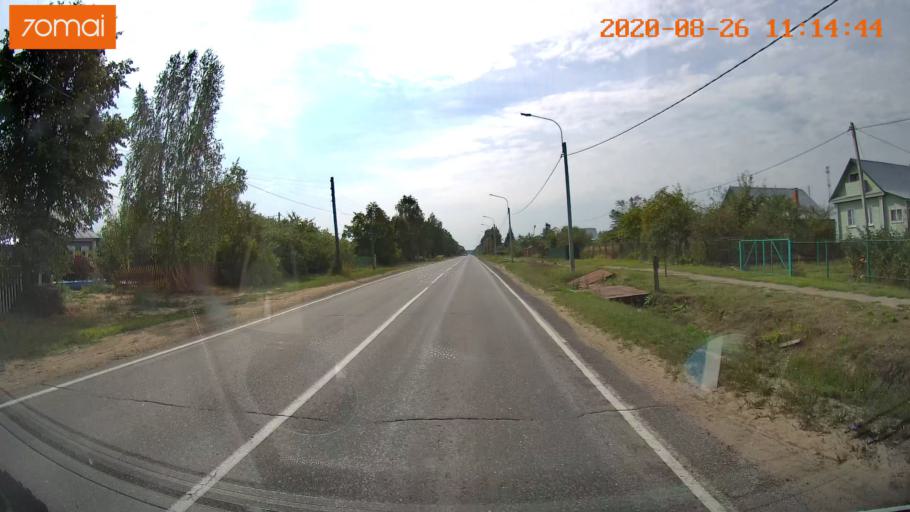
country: RU
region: Rjazan
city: Izhevskoye
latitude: 54.4460
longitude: 41.1162
